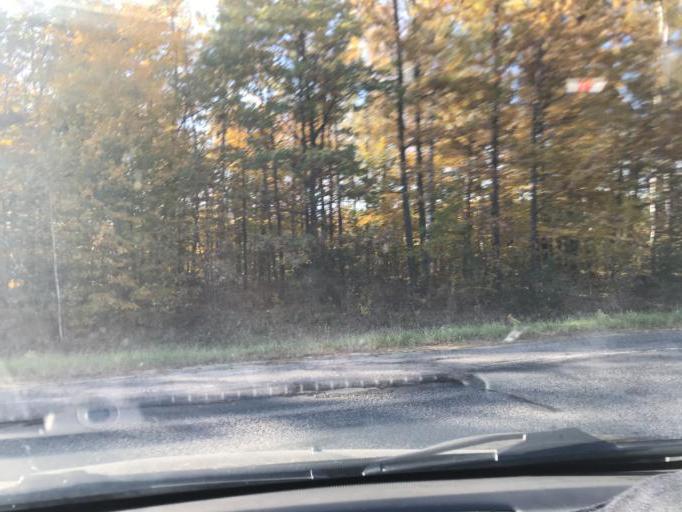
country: BY
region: Mogilev
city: Babruysk
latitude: 53.1087
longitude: 29.0558
